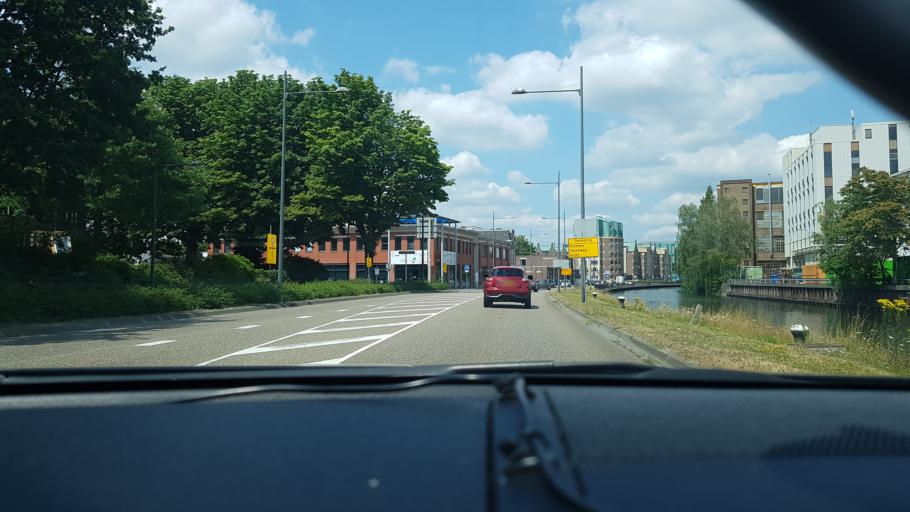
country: NL
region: North Brabant
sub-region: Gemeente Helmond
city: Helmond
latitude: 51.4742
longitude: 5.6527
